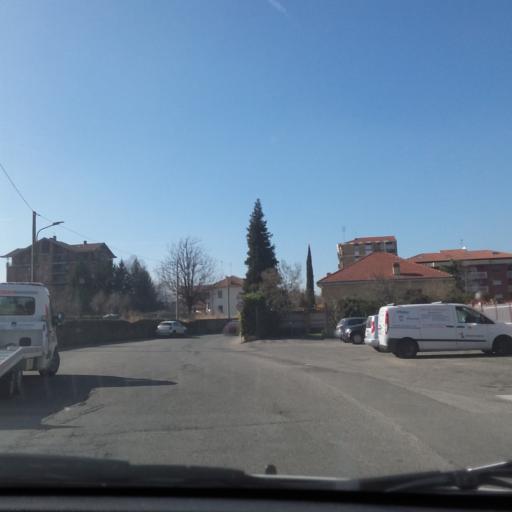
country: IT
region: Piedmont
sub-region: Provincia di Torino
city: Rivoli
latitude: 45.0749
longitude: 7.5113
